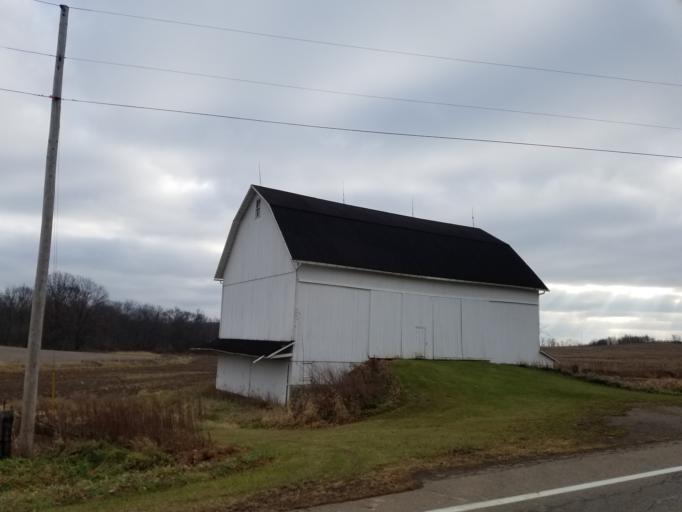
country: US
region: Ohio
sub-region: Knox County
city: Gambier
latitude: 40.4765
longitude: -82.3703
